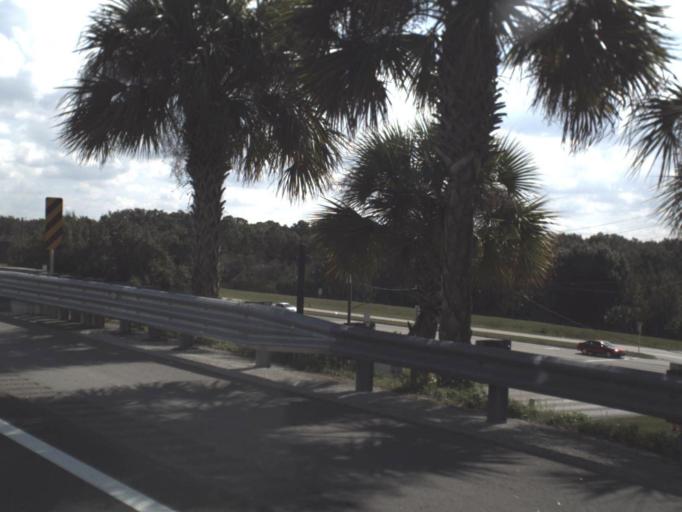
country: US
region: Florida
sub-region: Polk County
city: Fussels Corner
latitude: 28.0106
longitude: -81.8424
